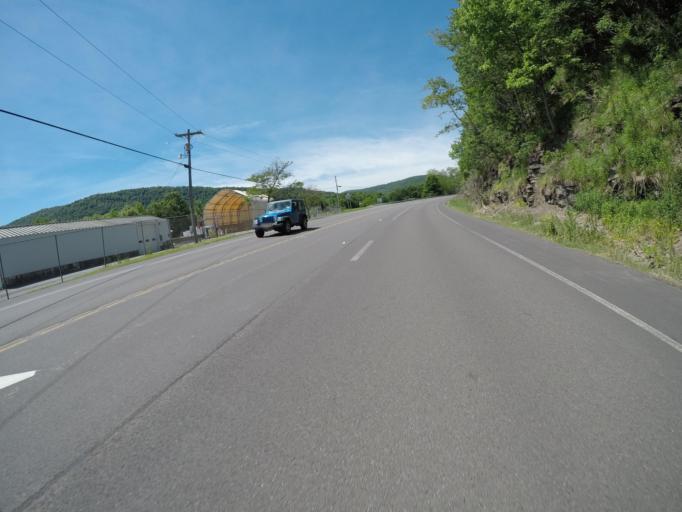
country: US
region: New York
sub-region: Delaware County
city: Walton
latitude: 42.1623
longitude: -75.0453
